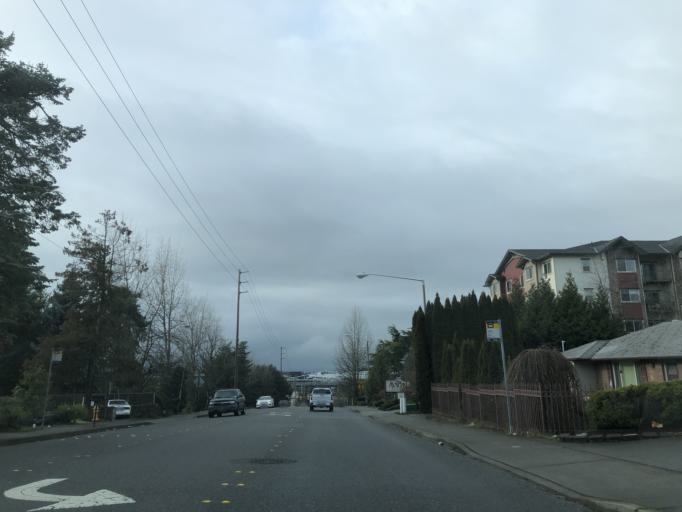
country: US
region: Washington
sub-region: King County
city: SeaTac
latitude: 47.4453
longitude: -122.2891
